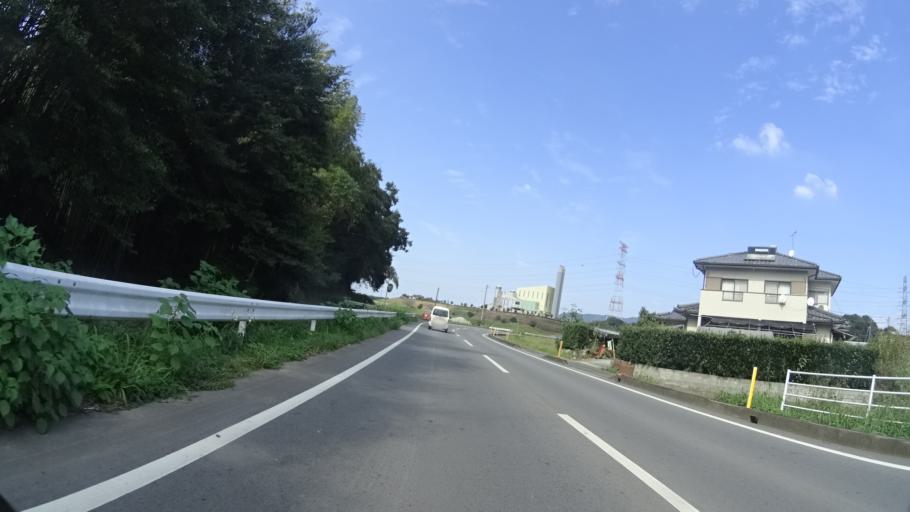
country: JP
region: Kumamoto
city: Matsubase
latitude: 32.6581
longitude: 130.7163
